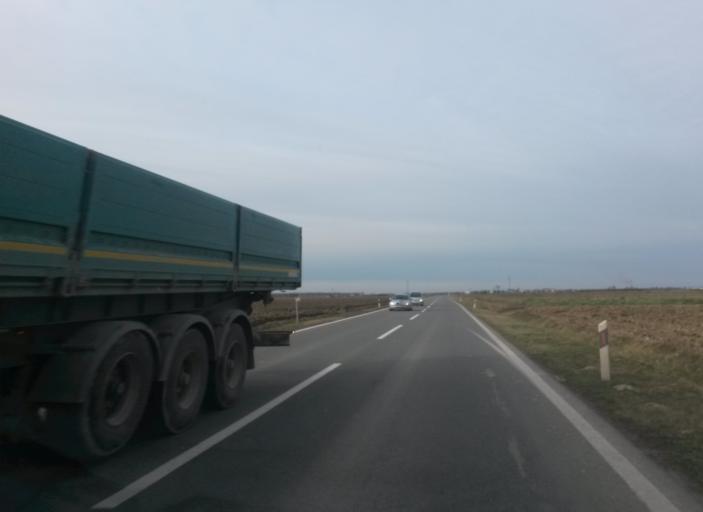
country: HR
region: Osjecko-Baranjska
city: Ovcara
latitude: 45.5052
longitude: 18.5470
